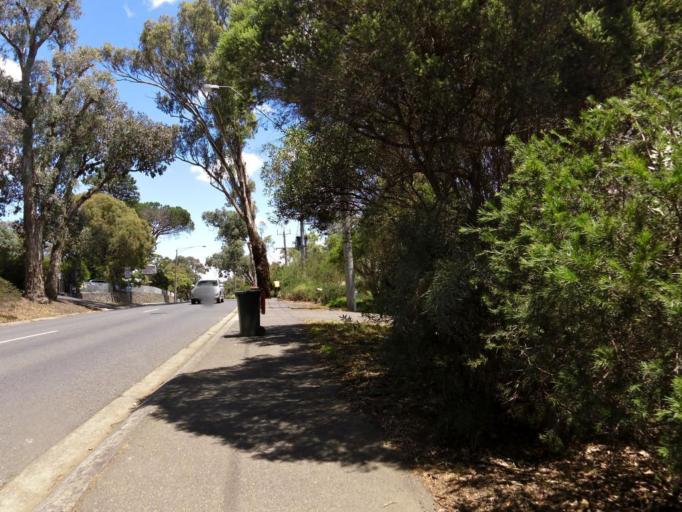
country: AU
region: Victoria
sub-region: Nillumbik
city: Research
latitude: -37.7023
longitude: 145.1846
